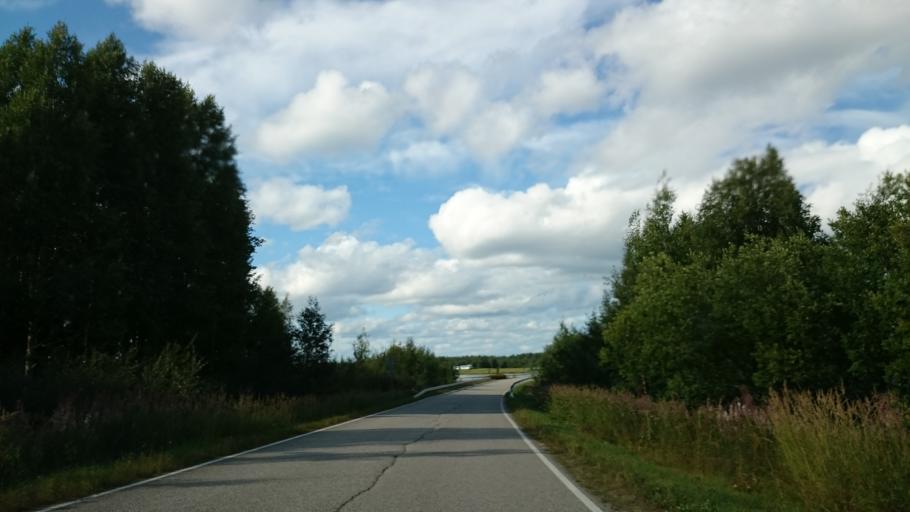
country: FI
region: Kainuu
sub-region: Kehys-Kainuu
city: Suomussalmi
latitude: 64.7375
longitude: 29.4397
